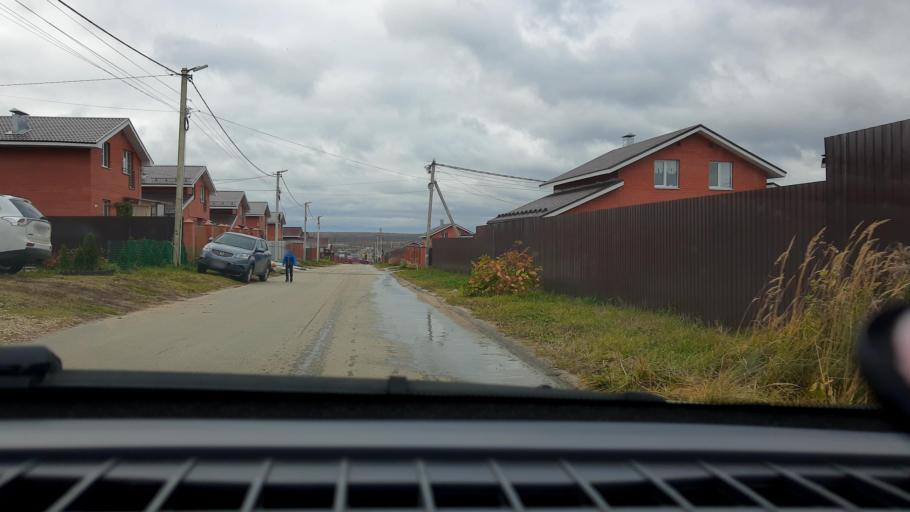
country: RU
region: Nizjnij Novgorod
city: Afonino
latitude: 56.2046
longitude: 44.1389
